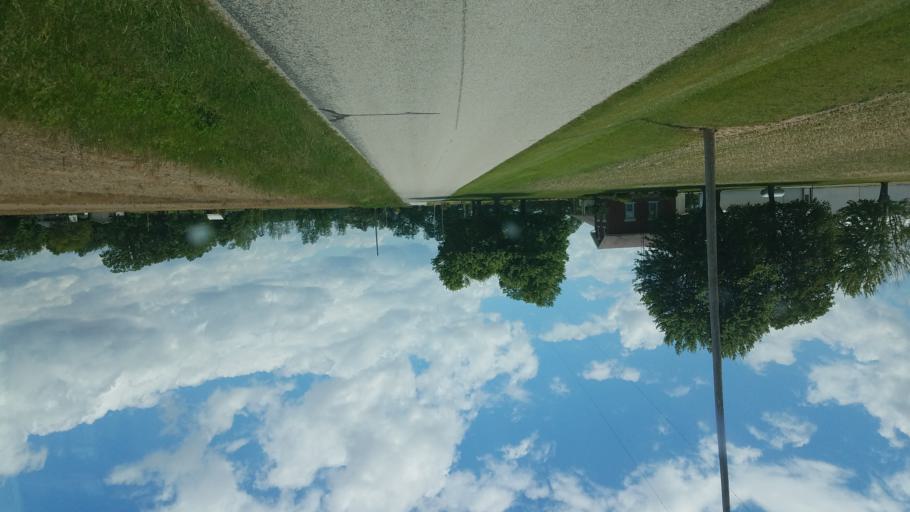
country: US
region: Ohio
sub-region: Huron County
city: Willard
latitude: 41.1331
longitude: -82.7439
